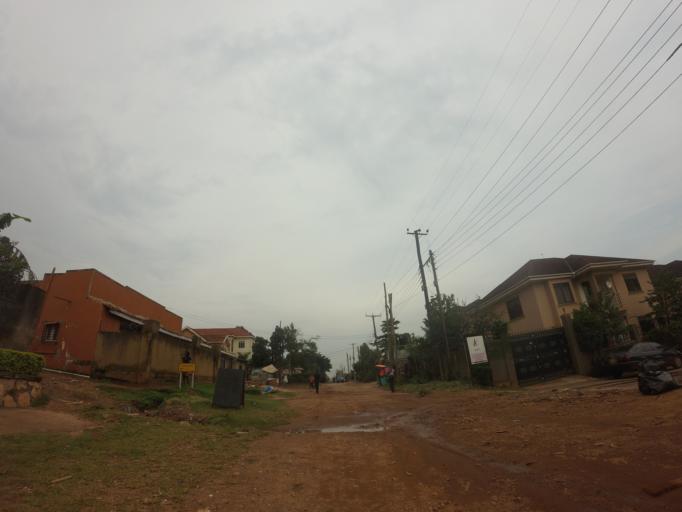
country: UG
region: Central Region
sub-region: Wakiso District
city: Kireka
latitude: 0.3425
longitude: 32.6176
